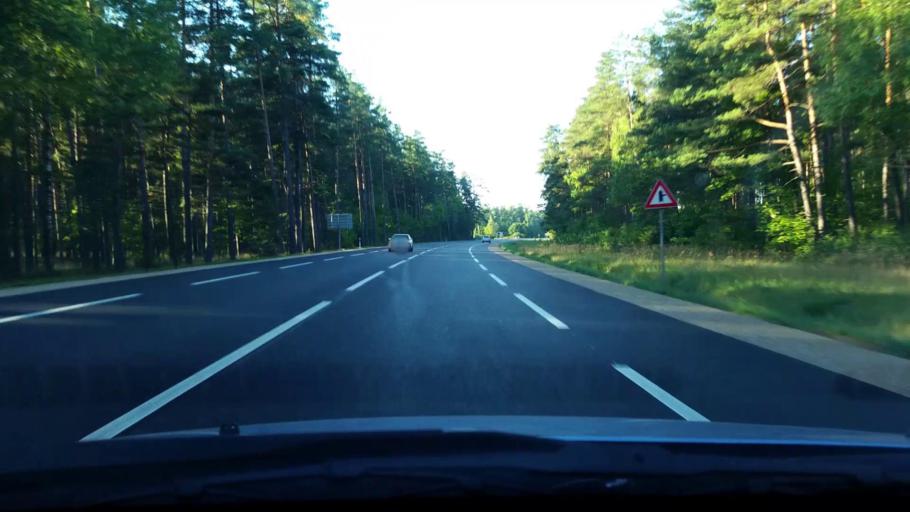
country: LV
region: Riga
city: Bergi
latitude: 57.0279
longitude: 24.3205
